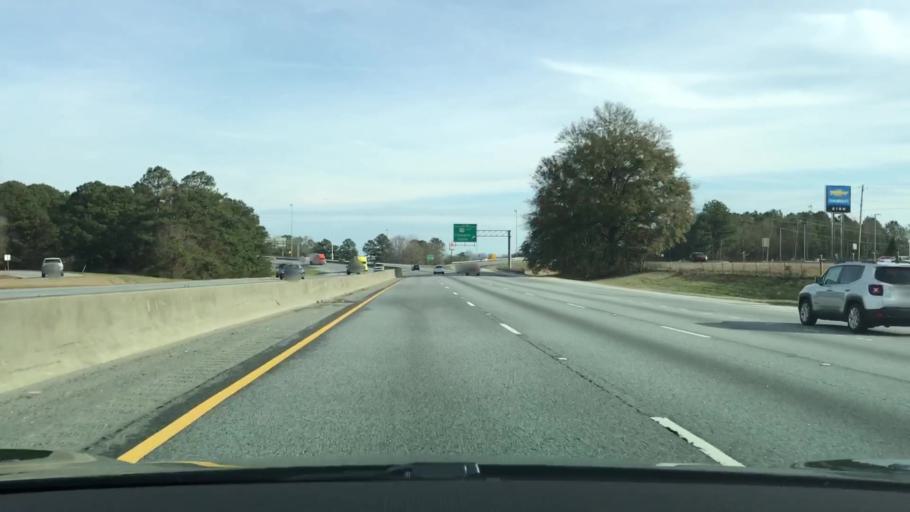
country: US
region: Georgia
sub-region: Newton County
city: Oxford
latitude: 33.6083
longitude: -83.8810
